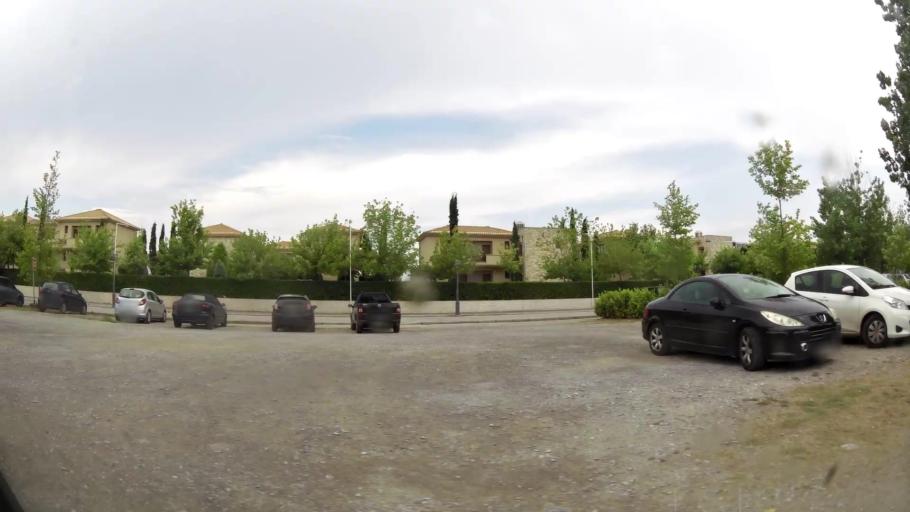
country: GR
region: Central Macedonia
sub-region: Nomos Pierias
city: Paralia
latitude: 40.2854
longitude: 22.6053
